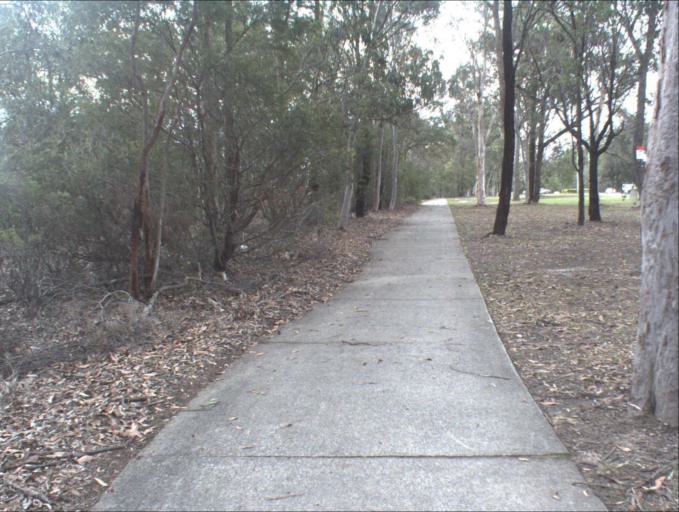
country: AU
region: Queensland
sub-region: Logan
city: Woodridge
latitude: -27.6751
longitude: 153.0770
